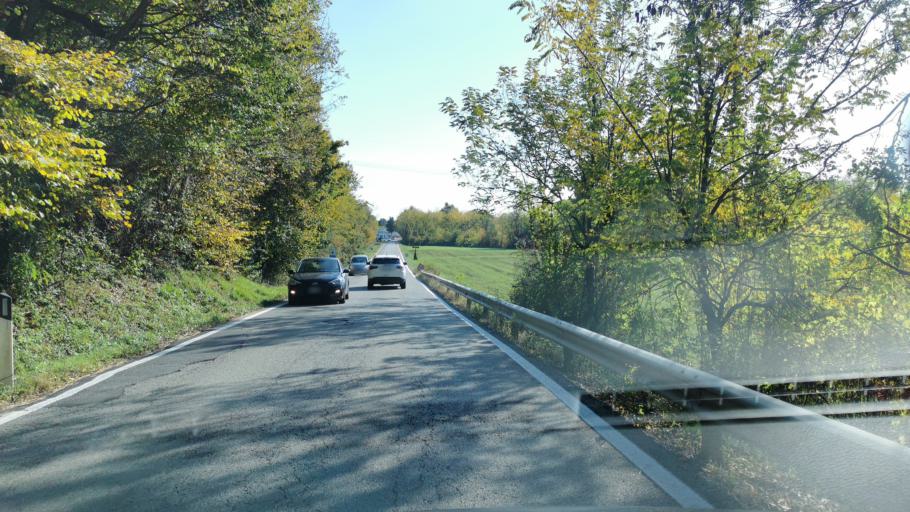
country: IT
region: Piedmont
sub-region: Provincia di Torino
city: Grosso
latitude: 45.2718
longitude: 7.5593
